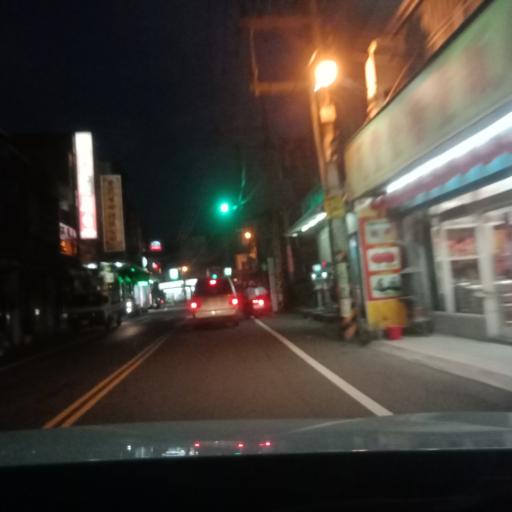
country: TW
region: Taiwan
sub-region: Hsinchu
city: Zhubei
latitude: 24.9072
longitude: 121.0478
